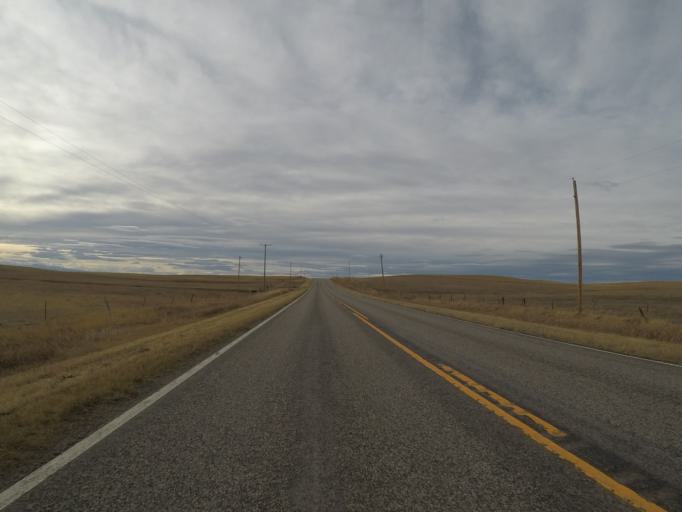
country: US
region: Montana
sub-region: Yellowstone County
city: Laurel
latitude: 45.8563
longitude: -108.7907
